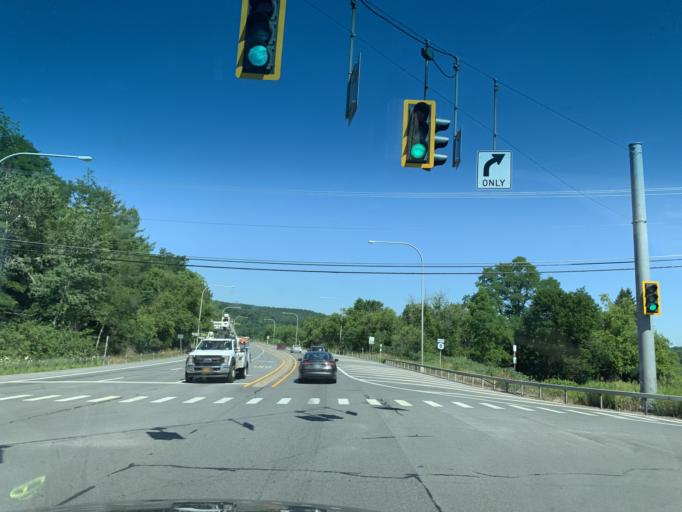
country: US
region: New York
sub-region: Delaware County
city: Sidney
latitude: 42.3092
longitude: -75.4044
